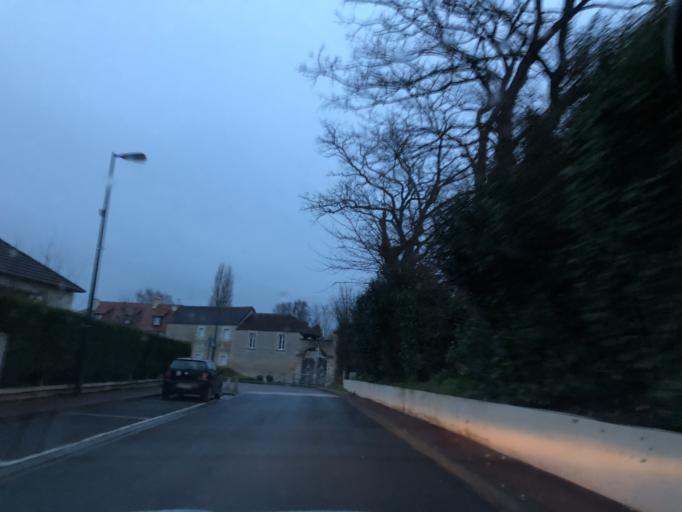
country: FR
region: Lower Normandy
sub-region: Departement du Calvados
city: Mathieu
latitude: 49.2553
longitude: -0.3717
